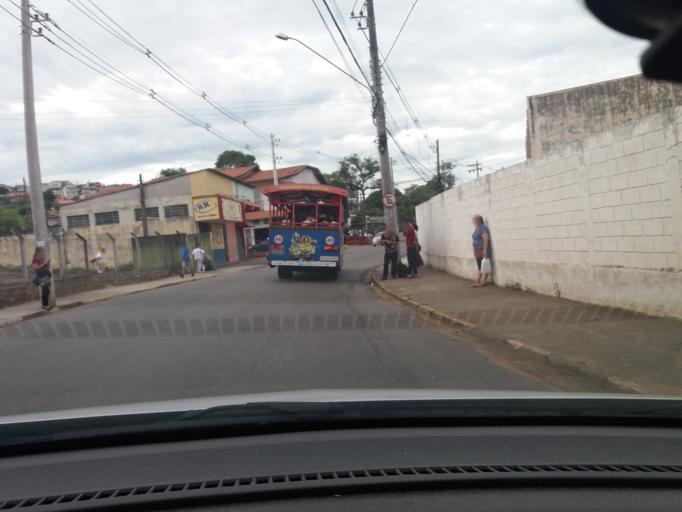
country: BR
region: Sao Paulo
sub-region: Bom Jesus Dos Perdoes
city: Bom Jesus dos Perdoes
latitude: -23.1269
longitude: -46.4701
